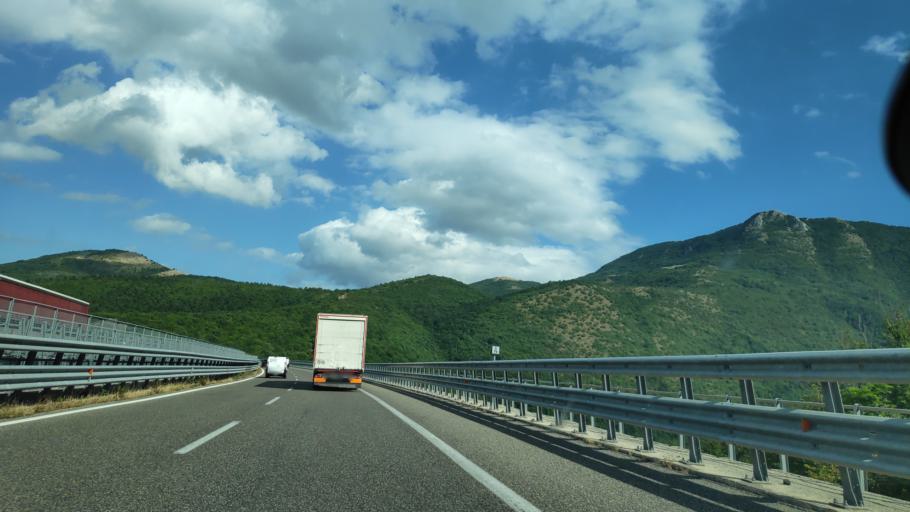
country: IT
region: Campania
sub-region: Provincia di Salerno
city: Pertosa
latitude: 40.5309
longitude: 15.4280
